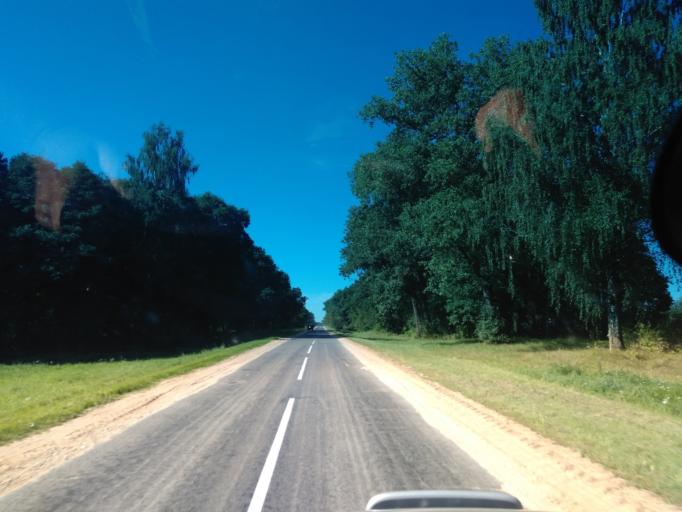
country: BY
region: Minsk
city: Stan'kava
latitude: 53.6371
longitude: 27.2842
